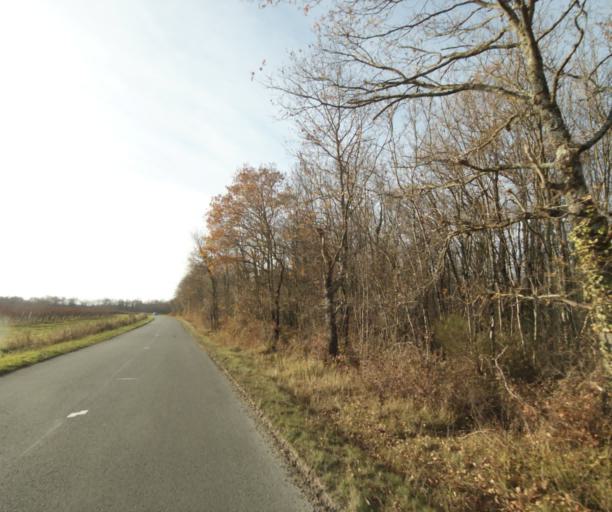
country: FR
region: Poitou-Charentes
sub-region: Departement de la Charente-Maritime
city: Chaniers
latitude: 45.7515
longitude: -0.5236
